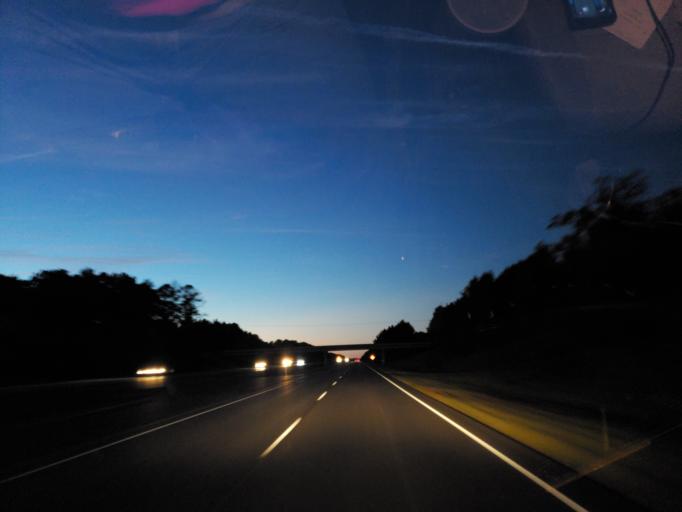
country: US
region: Mississippi
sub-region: Clarke County
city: Quitman
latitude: 32.0751
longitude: -88.6882
